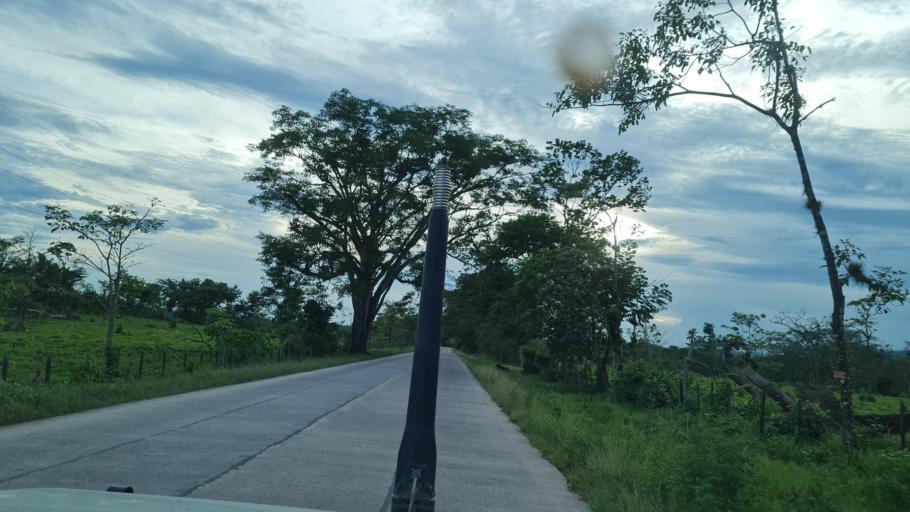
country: NI
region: Atlantico Norte (RAAN)
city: Siuna
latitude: 13.6835
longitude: -84.5880
